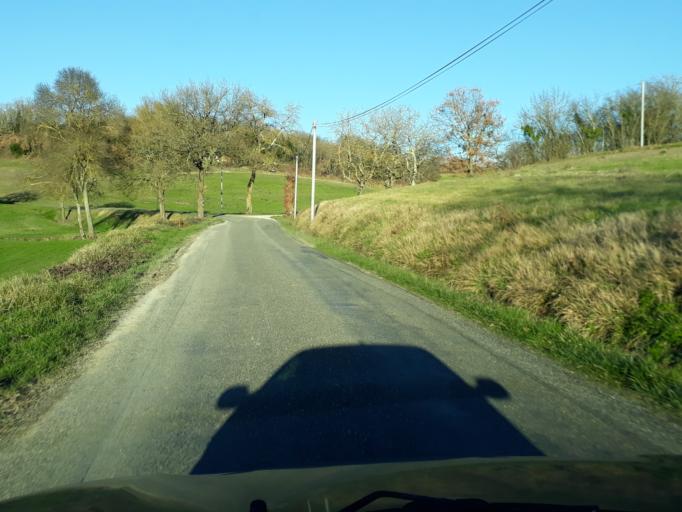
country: FR
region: Midi-Pyrenees
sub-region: Departement du Gers
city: Pavie
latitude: 43.6232
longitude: 0.6583
